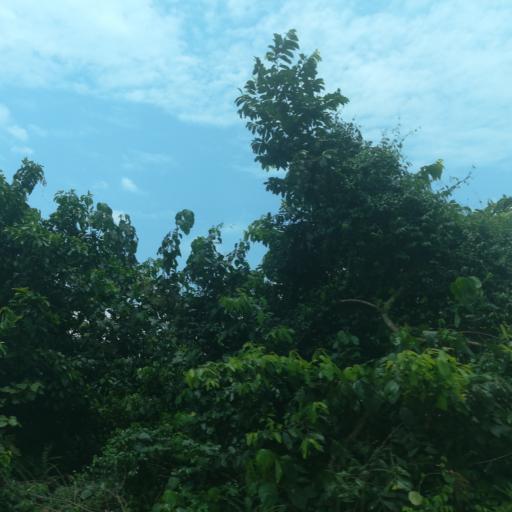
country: NG
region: Lagos
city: Ejirin
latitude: 6.6627
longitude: 3.8107
